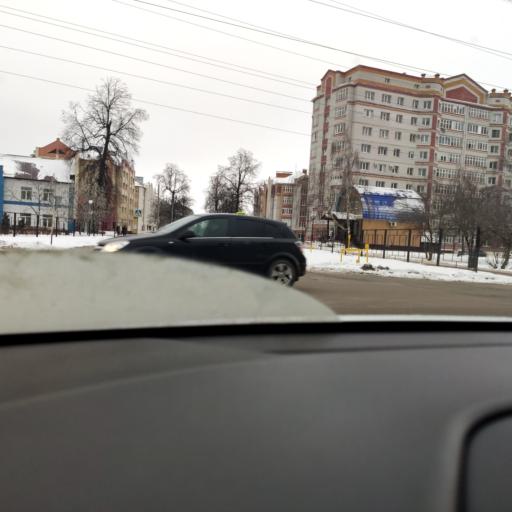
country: RU
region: Tatarstan
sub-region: Zelenodol'skiy Rayon
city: Zelenodolsk
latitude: 55.8512
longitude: 48.4864
